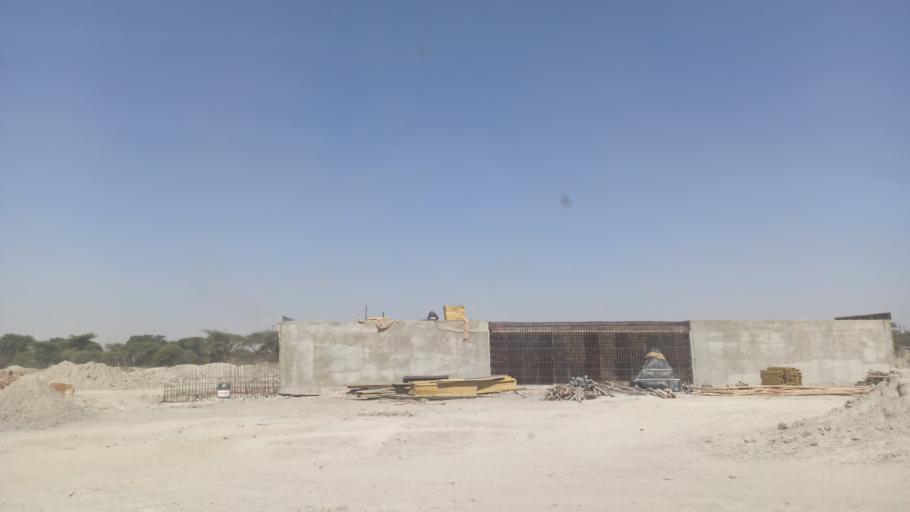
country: ET
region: Oromiya
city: Ziway
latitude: 7.7013
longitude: 38.6410
